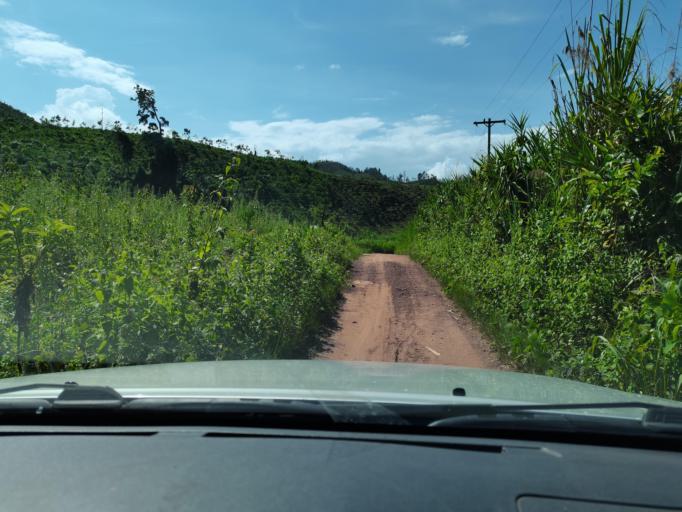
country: LA
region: Loungnamtha
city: Muang Nale
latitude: 20.5616
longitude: 101.0588
